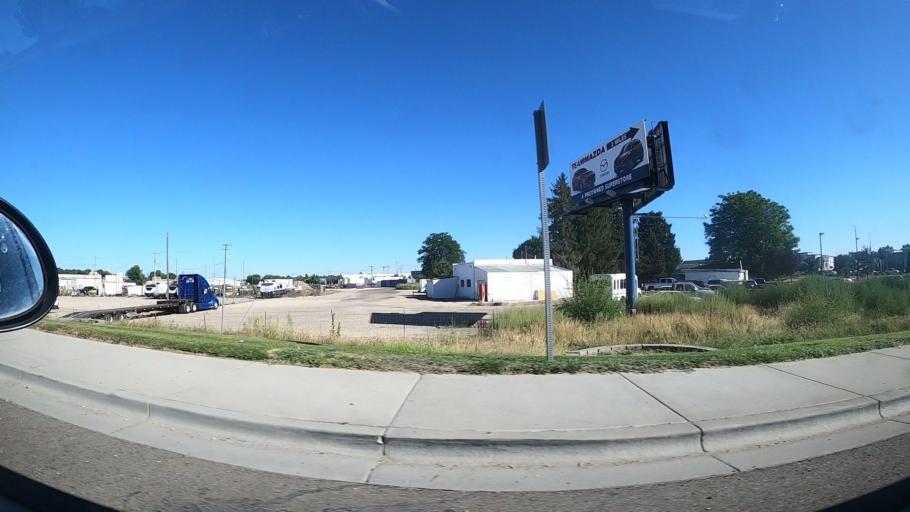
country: US
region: Idaho
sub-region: Canyon County
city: Nampa
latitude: 43.6050
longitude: -116.6022
